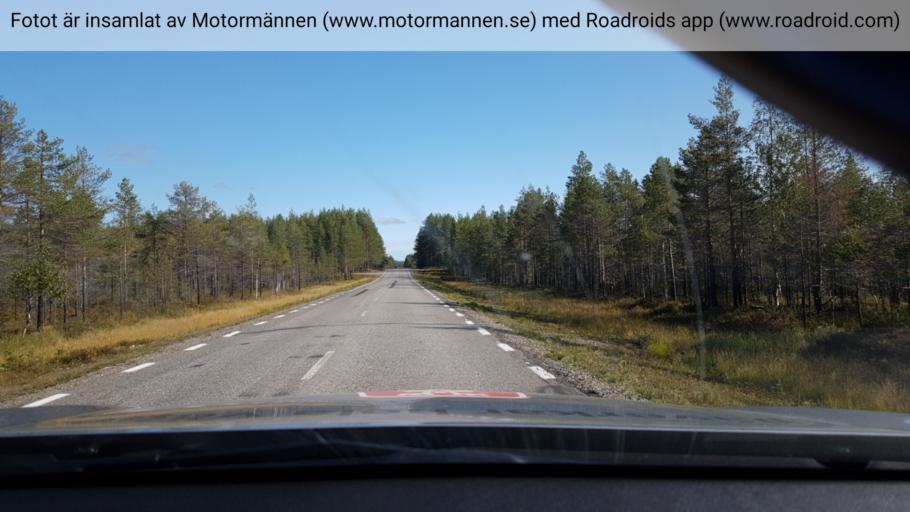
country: SE
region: Vaesterbotten
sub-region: Norsjo Kommun
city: Norsjoe
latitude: 65.1348
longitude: 19.2743
